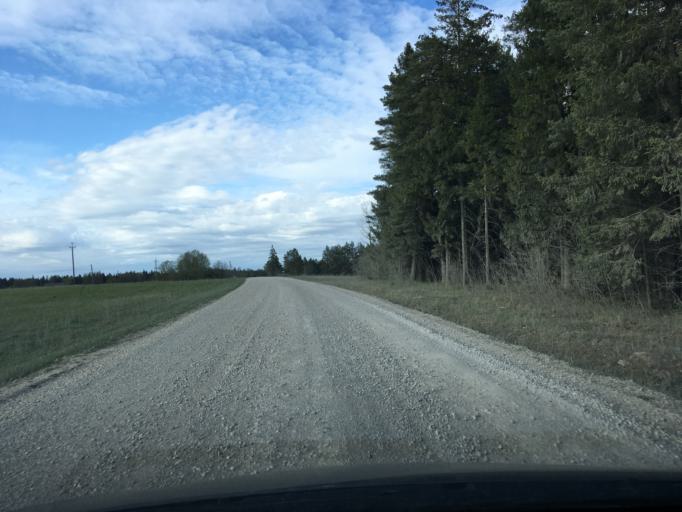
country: EE
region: Raplamaa
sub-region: Maerjamaa vald
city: Marjamaa
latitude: 58.9456
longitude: 24.3182
